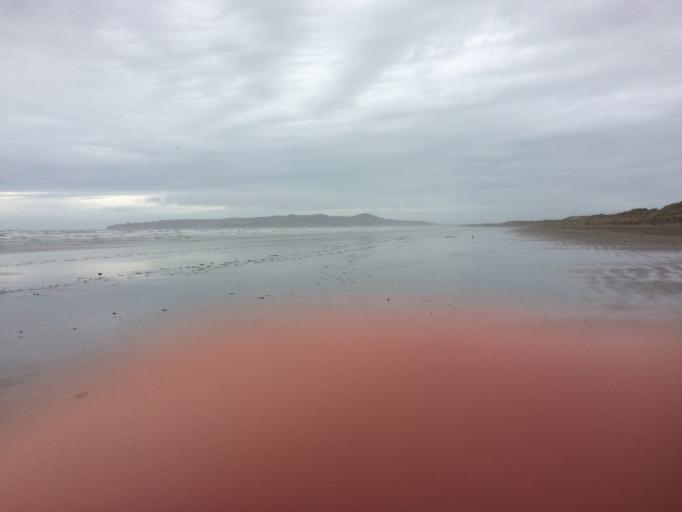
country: IE
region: Leinster
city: Portmarnock
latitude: 53.4267
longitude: -6.1230
